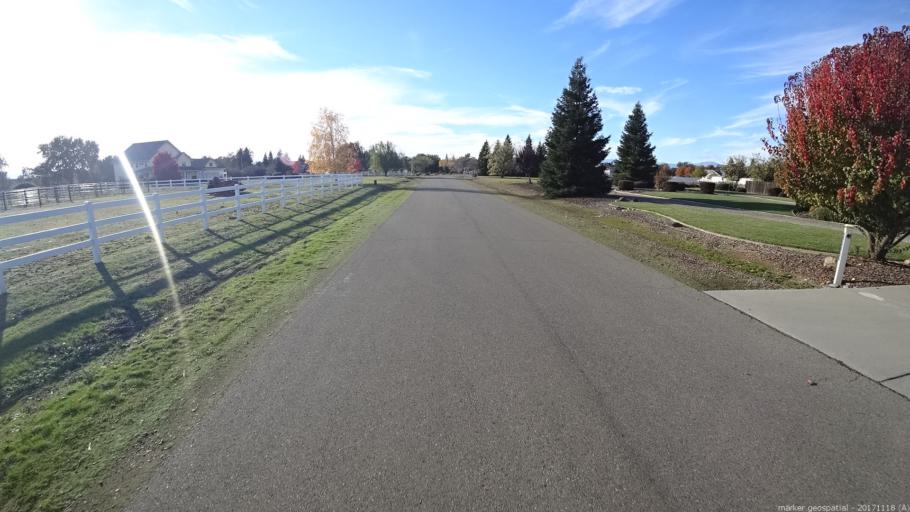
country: US
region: California
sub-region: Shasta County
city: Cottonwood
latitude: 40.3764
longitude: -122.3441
